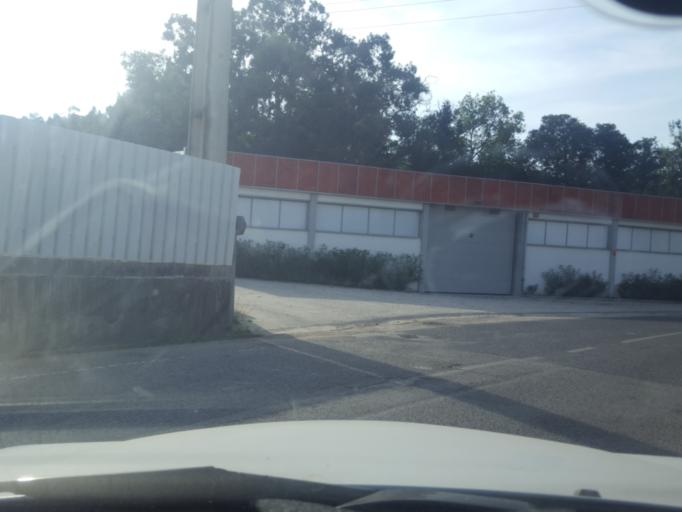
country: PT
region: Leiria
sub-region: Leiria
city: Leiria
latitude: 39.7137
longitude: -8.7868
